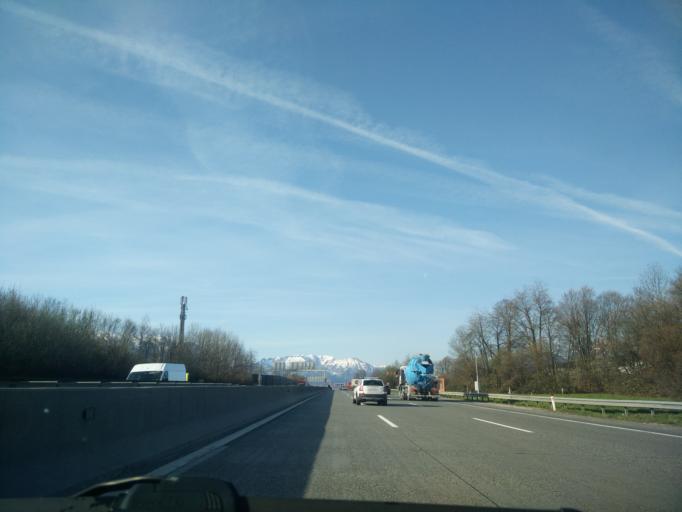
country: DE
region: Bavaria
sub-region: Upper Bavaria
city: Freilassing
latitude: 47.8181
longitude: 13.0039
